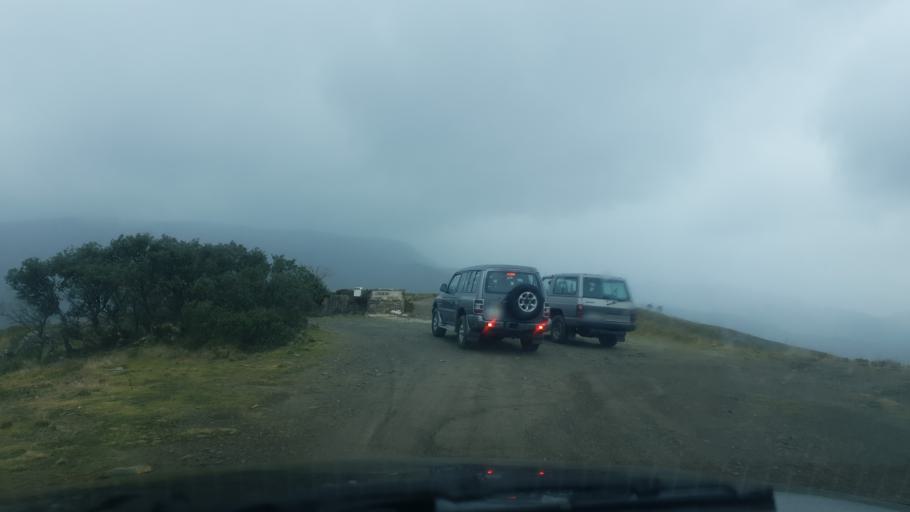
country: PT
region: Viseu
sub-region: Sao Pedro do Sul
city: Sao Pedro do Sul
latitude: 40.8527
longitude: -8.1136
